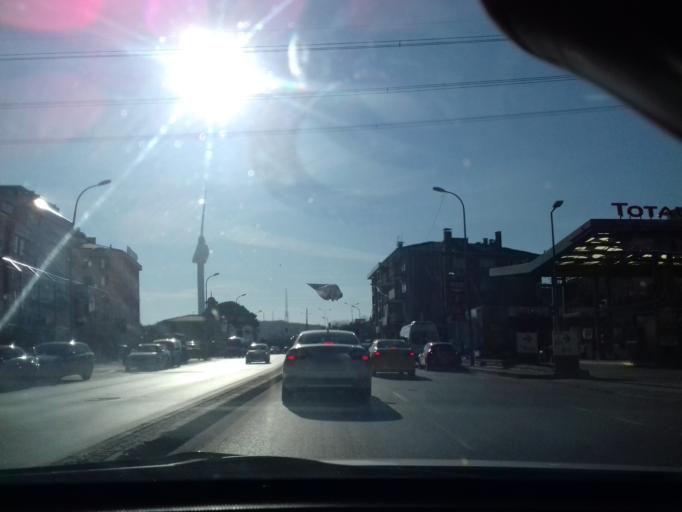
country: TR
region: Istanbul
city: Umraniye
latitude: 41.0240
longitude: 29.0822
